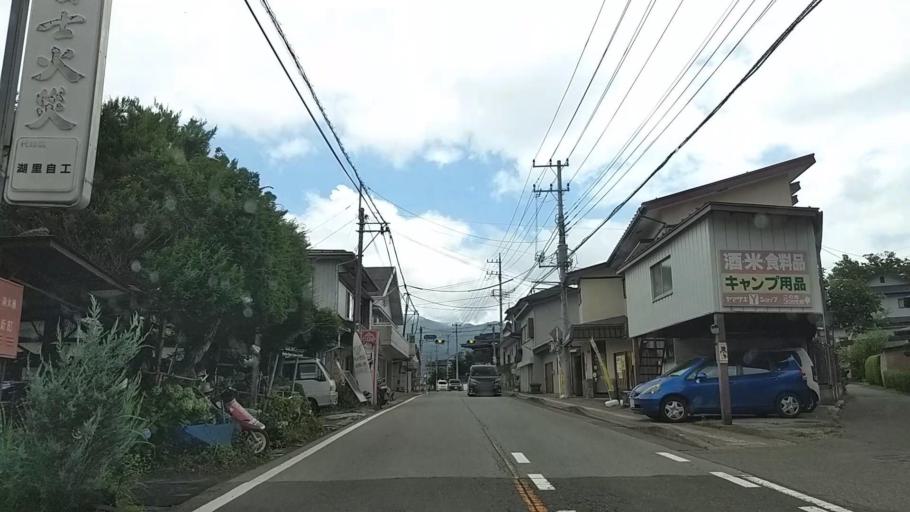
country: JP
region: Yamanashi
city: Fujikawaguchiko
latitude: 35.5043
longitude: 138.7389
